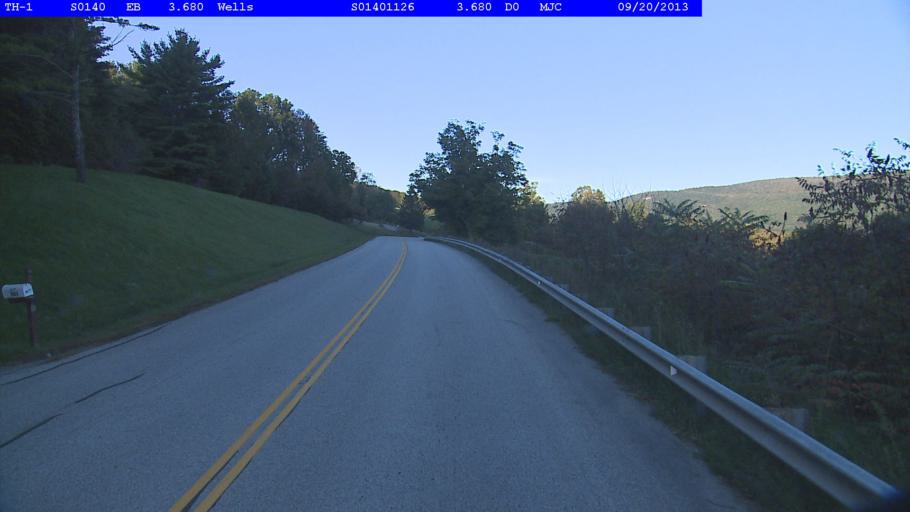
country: US
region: New York
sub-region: Washington County
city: Granville
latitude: 43.4141
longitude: -73.1367
